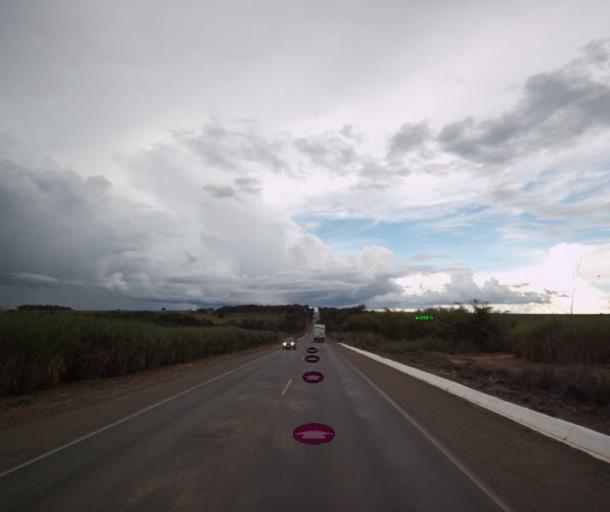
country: BR
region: Goias
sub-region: Itapaci
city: Itapaci
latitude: -14.9165
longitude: -49.3575
